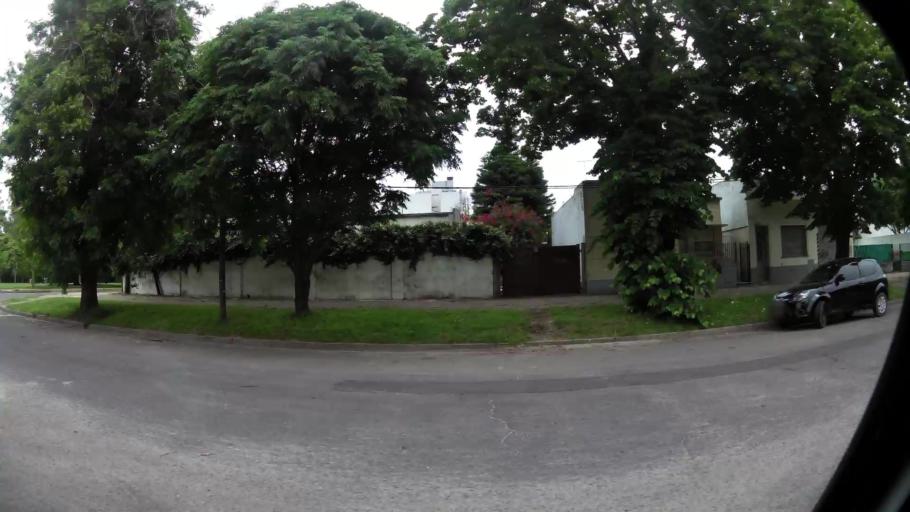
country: AR
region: Buenos Aires
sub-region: Partido de La Plata
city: La Plata
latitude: -34.9316
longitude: -57.9685
